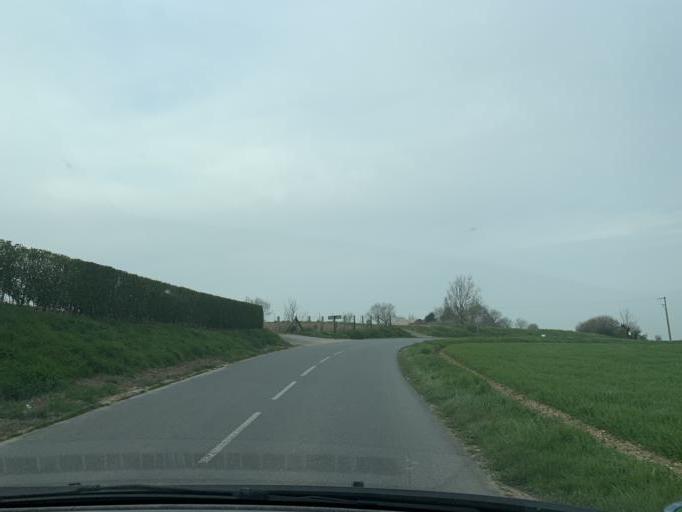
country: FR
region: Nord-Pas-de-Calais
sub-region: Departement du Pas-de-Calais
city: Samer
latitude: 50.6723
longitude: 1.7544
